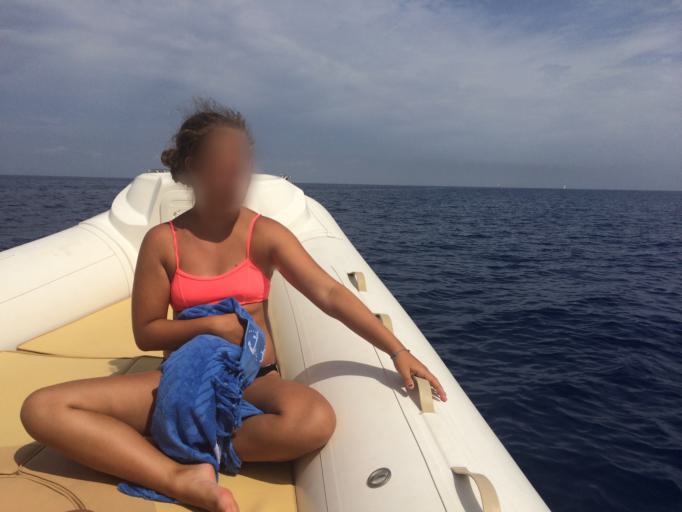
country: IT
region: Tuscany
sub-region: Provincia di Livorno
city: Capraia Isola
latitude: 43.0465
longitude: 9.7933
